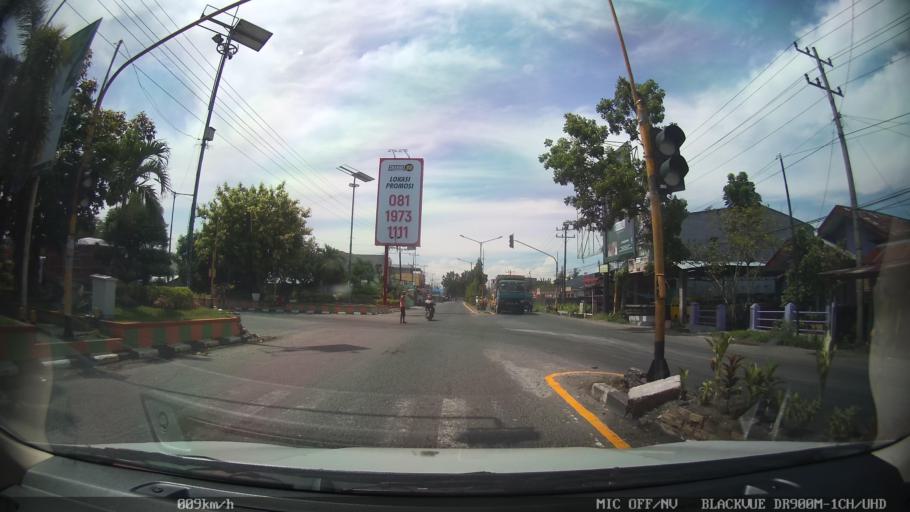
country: ID
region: North Sumatra
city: Binjai
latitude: 3.6506
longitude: 98.5101
